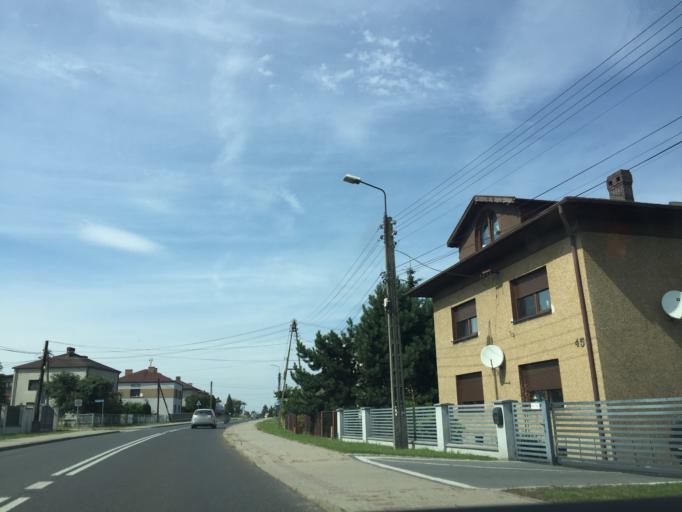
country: PL
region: Silesian Voivodeship
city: Gorzyczki
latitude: 49.9495
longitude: 18.4039
